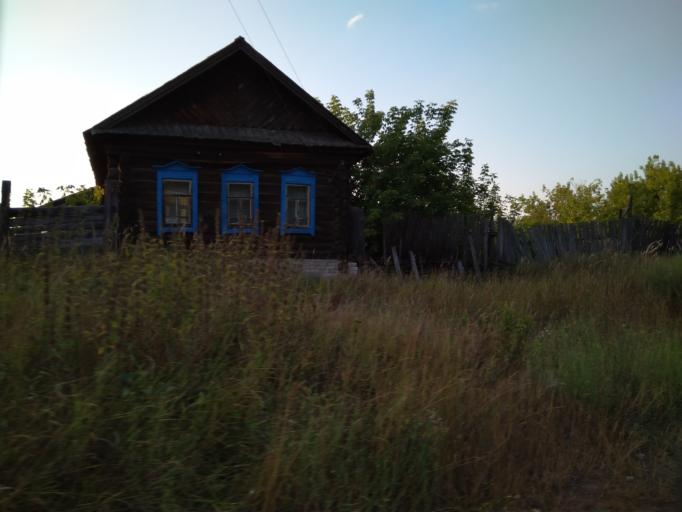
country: RU
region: Ulyanovsk
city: Staraya Mayna
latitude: 54.6455
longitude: 49.0508
